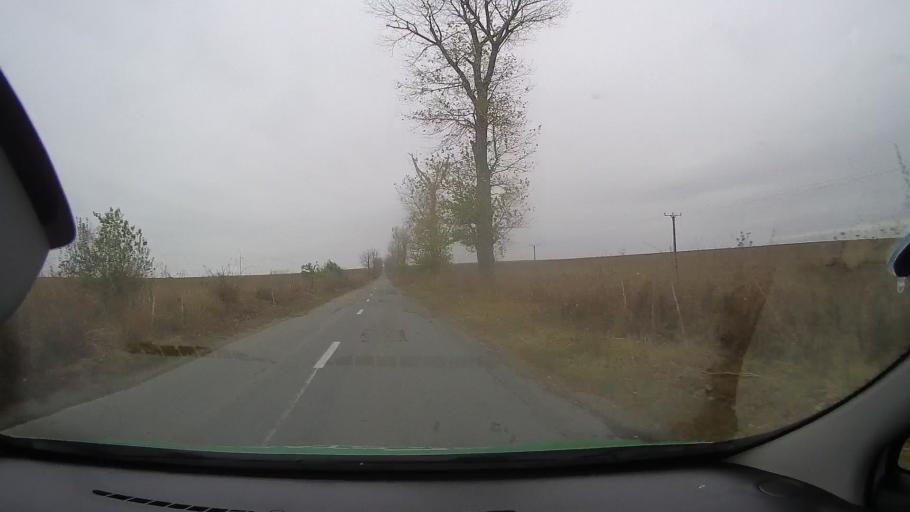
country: RO
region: Constanta
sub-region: Comuna Pantelimon
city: Pantelimon
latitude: 44.5542
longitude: 28.3261
